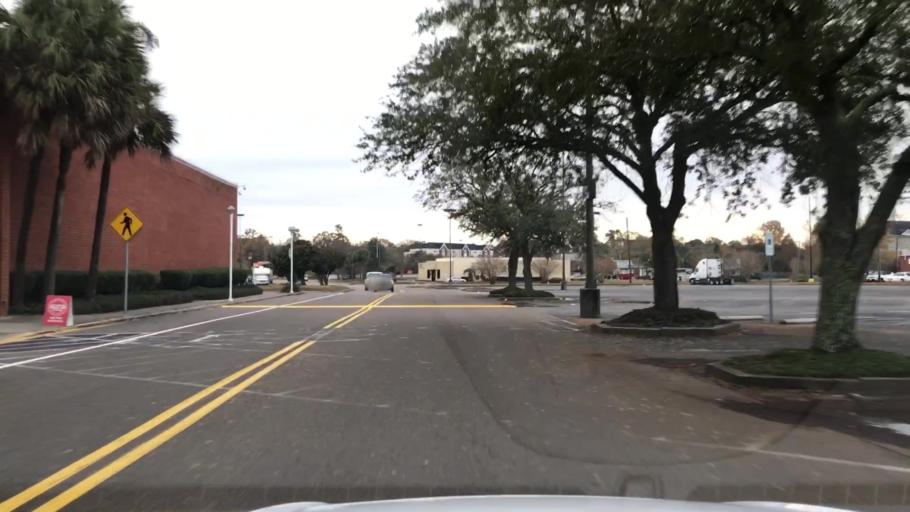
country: US
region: South Carolina
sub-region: Berkeley County
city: Hanahan
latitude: 32.9433
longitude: -80.0469
